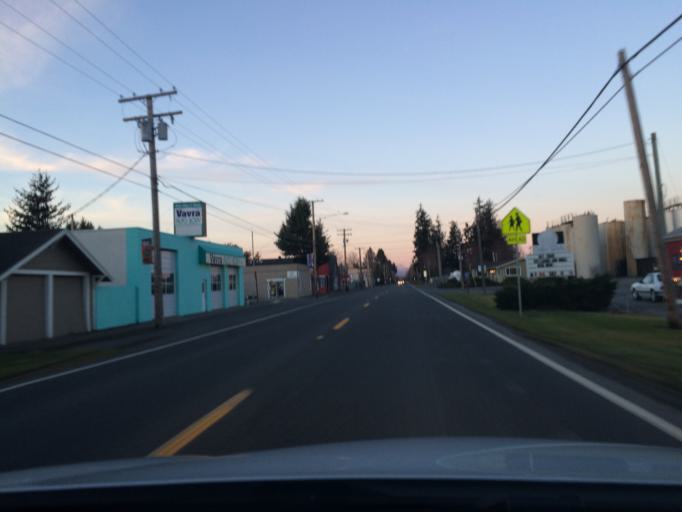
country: US
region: Washington
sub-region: Whatcom County
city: Nooksack
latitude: 48.9254
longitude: -122.3218
